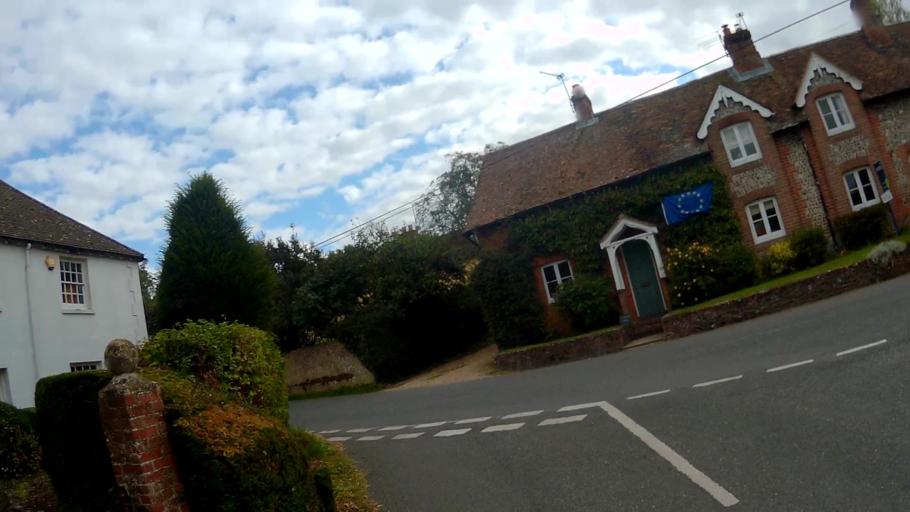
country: GB
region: England
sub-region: Hampshire
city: Kings Worthy
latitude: 51.1522
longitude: -1.3248
